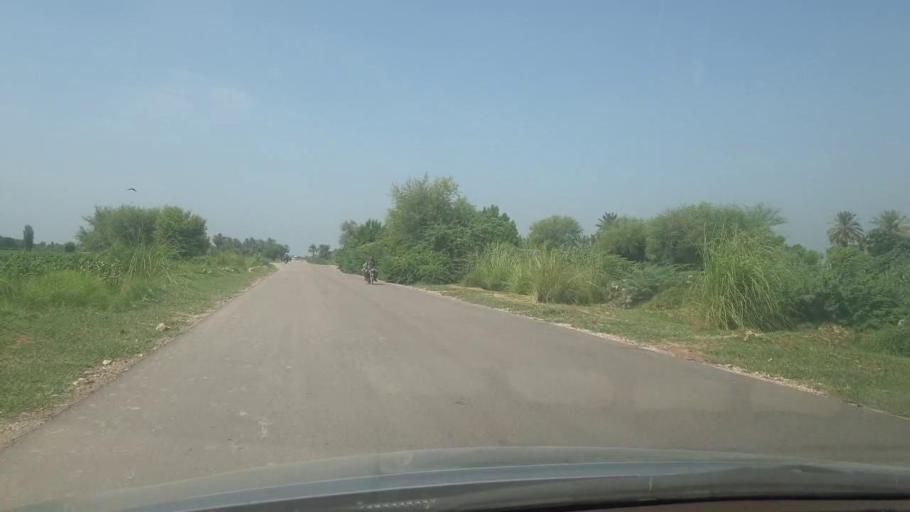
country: PK
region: Sindh
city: Ranipur
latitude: 27.2460
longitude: 68.5786
